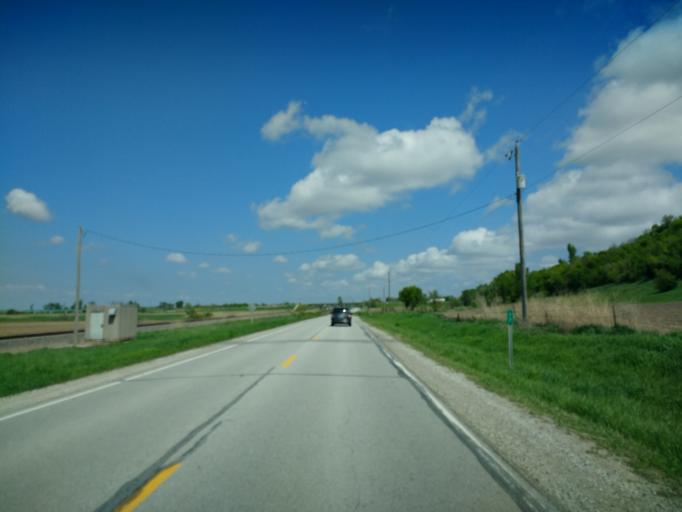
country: US
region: Iowa
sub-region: Harrison County
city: Missouri Valley
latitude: 41.4886
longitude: -95.8878
